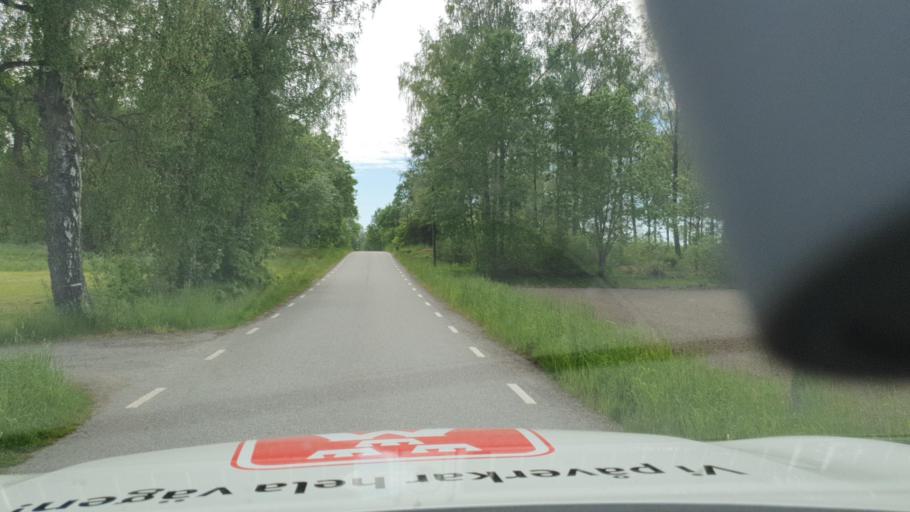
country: SE
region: Vaestra Goetaland
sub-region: Vanersborgs Kommun
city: Vargon
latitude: 58.2680
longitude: 12.5042
